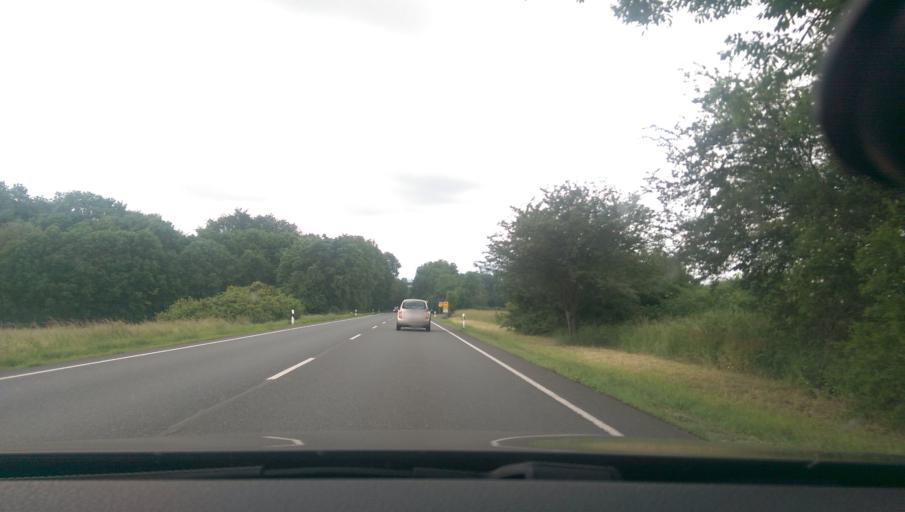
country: DE
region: Thuringia
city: Rockhausen
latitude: 50.9175
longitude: 11.0347
